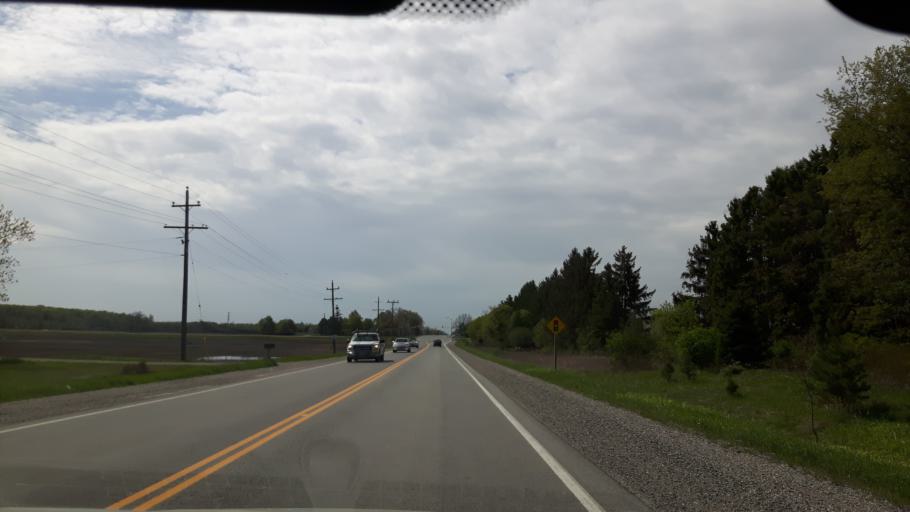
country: CA
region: Ontario
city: London
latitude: 43.1010
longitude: -81.3211
